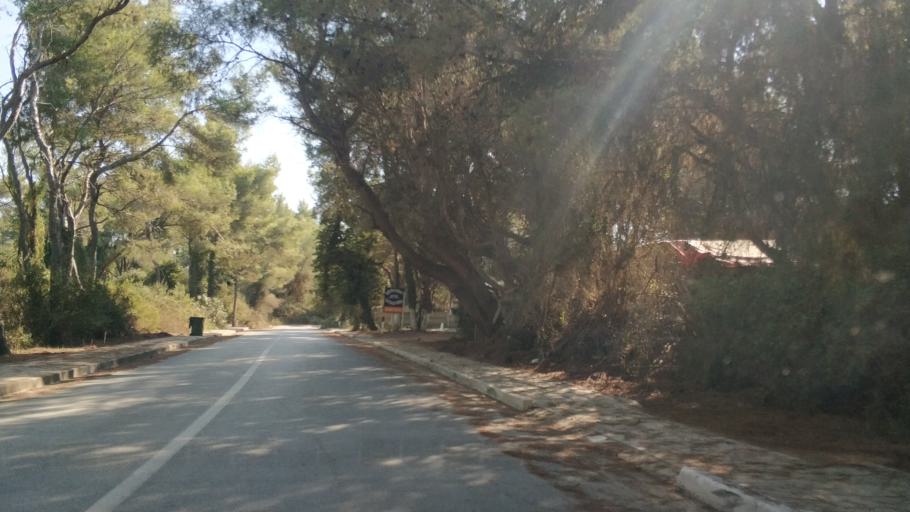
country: AL
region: Fier
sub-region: Rrethi i Lushnjes
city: Divjake
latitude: 40.9642
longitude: 19.4774
